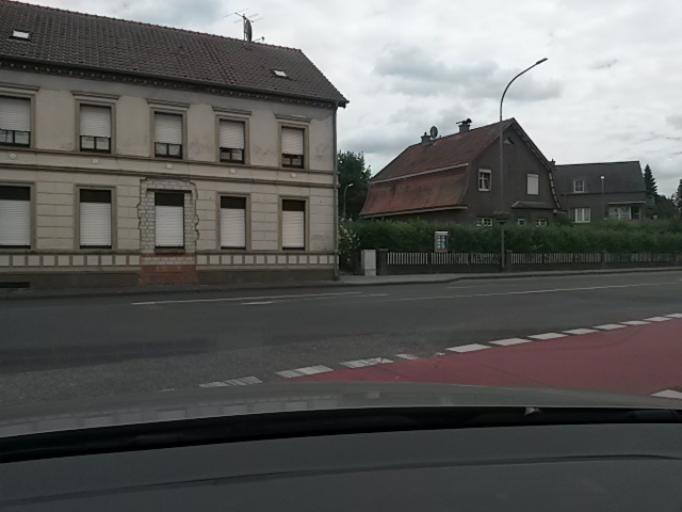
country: DE
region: North Rhine-Westphalia
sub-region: Regierungsbezirk Dusseldorf
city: Nettetal
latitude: 51.2689
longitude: 6.2708
